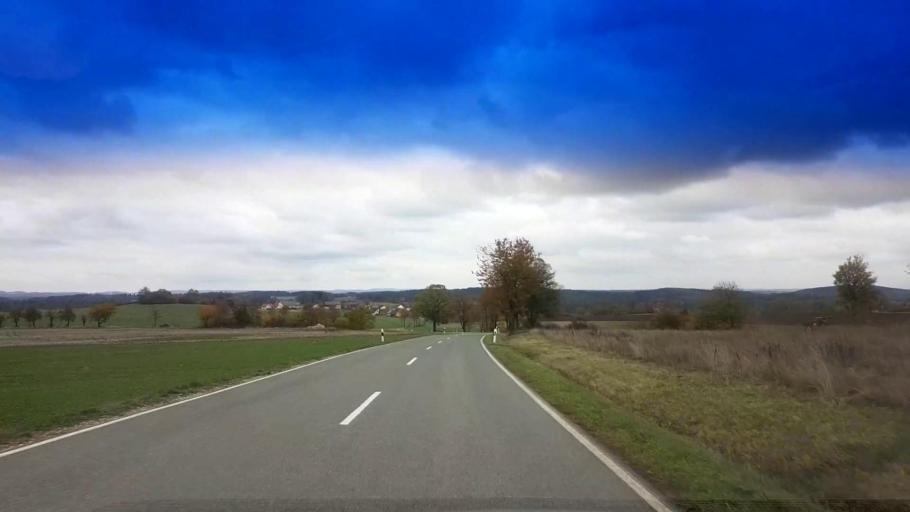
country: DE
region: Bavaria
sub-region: Upper Franconia
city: Poxdorf
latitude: 49.9407
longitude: 11.1123
